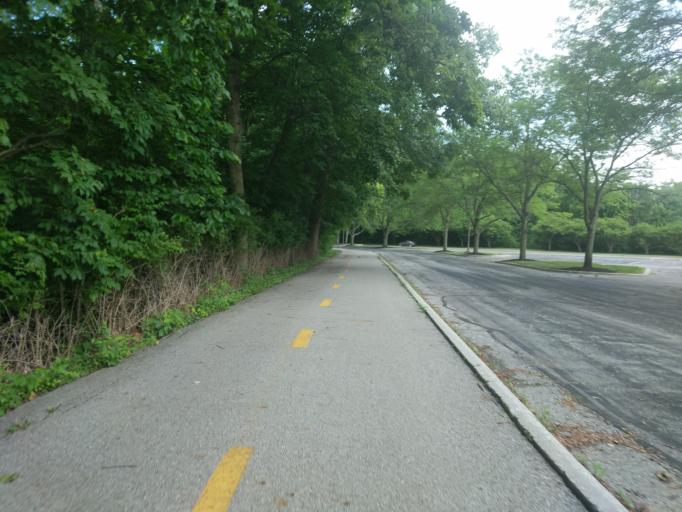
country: US
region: Ohio
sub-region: Franklin County
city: Huber Ridge
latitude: 40.0803
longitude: -82.9194
